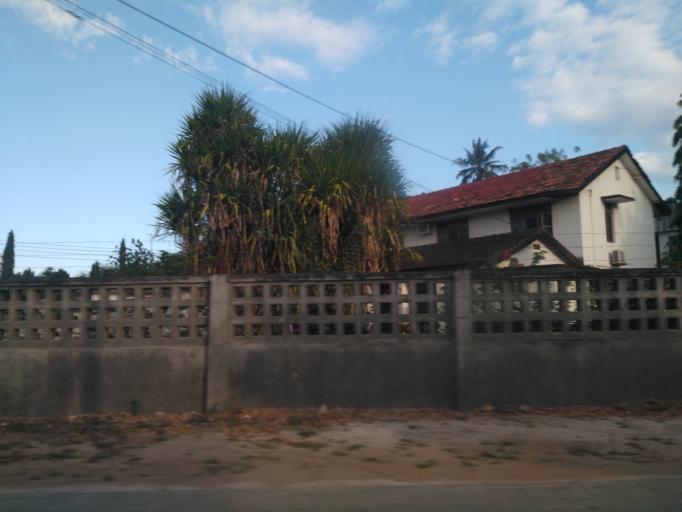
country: TZ
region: Dar es Salaam
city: Magomeni
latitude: -6.7824
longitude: 39.2709
